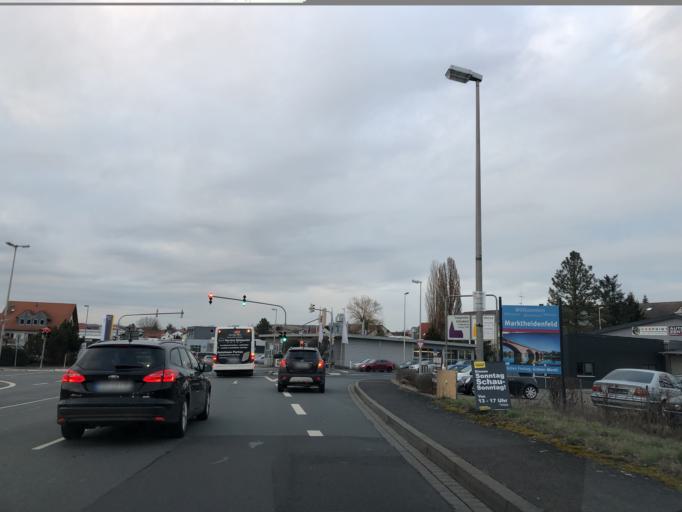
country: DE
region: Bavaria
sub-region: Regierungsbezirk Unterfranken
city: Marktheidenfeld
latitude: 49.8393
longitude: 9.6073
